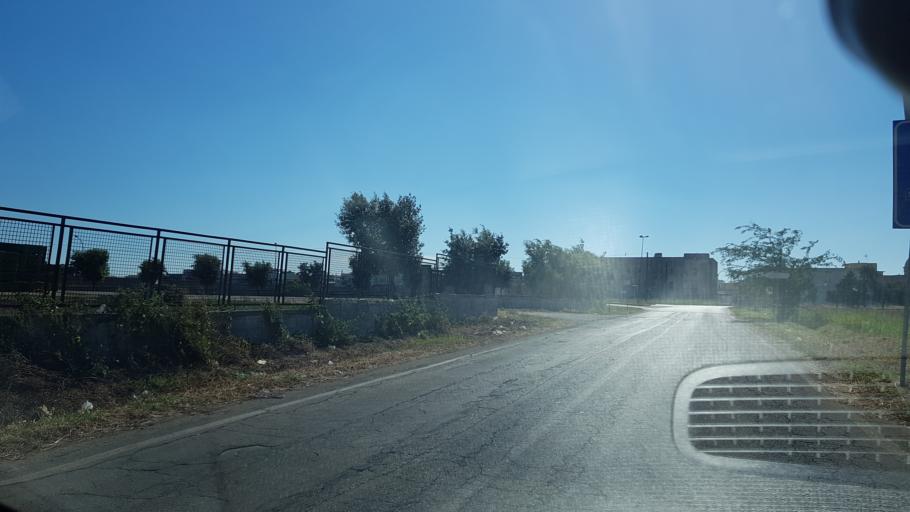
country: IT
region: Apulia
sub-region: Provincia di Brindisi
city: Mesagne
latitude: 40.5574
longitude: 17.8247
